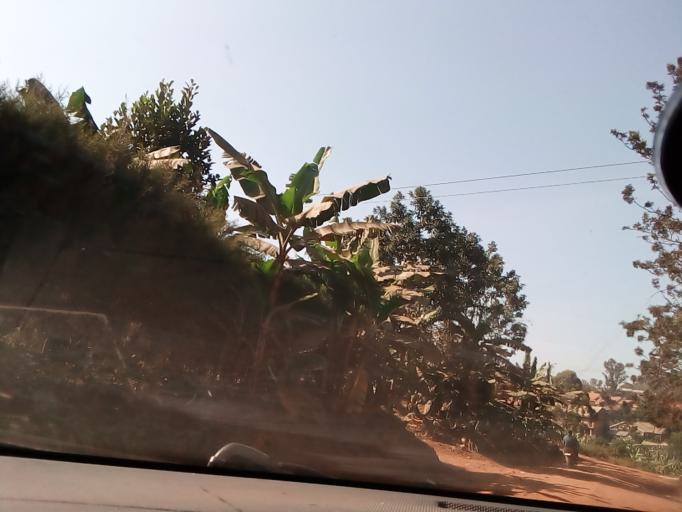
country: UG
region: Central Region
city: Masaka
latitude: -0.3403
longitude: 31.7314
